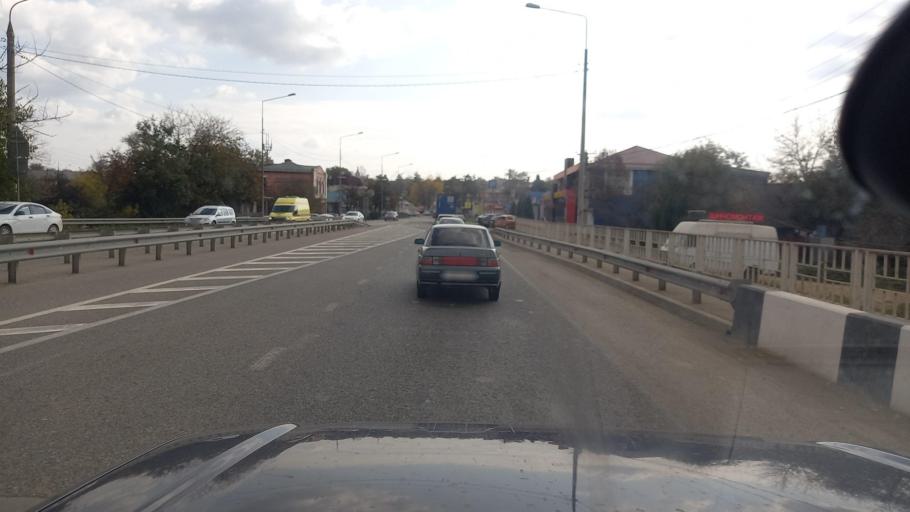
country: RU
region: Krasnodarskiy
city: Kholmskiy
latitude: 44.8444
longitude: 38.3914
